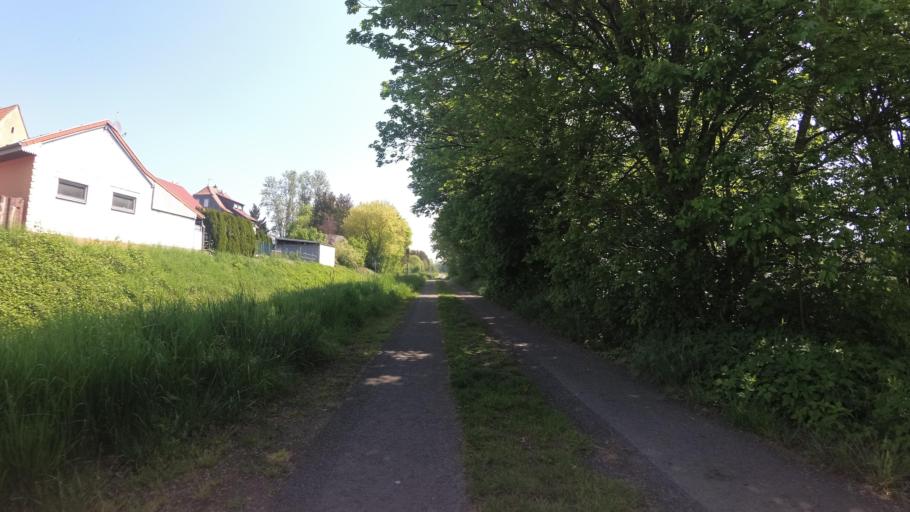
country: DE
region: Rheinland-Pfalz
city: Steinwenden
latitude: 49.4543
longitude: 7.5282
